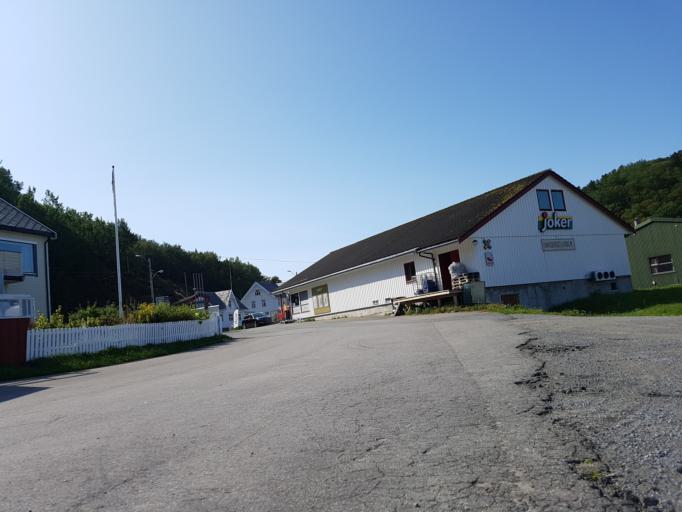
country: NO
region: Sor-Trondelag
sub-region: Agdenes
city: Lensvik
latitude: 63.6328
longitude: 9.8283
